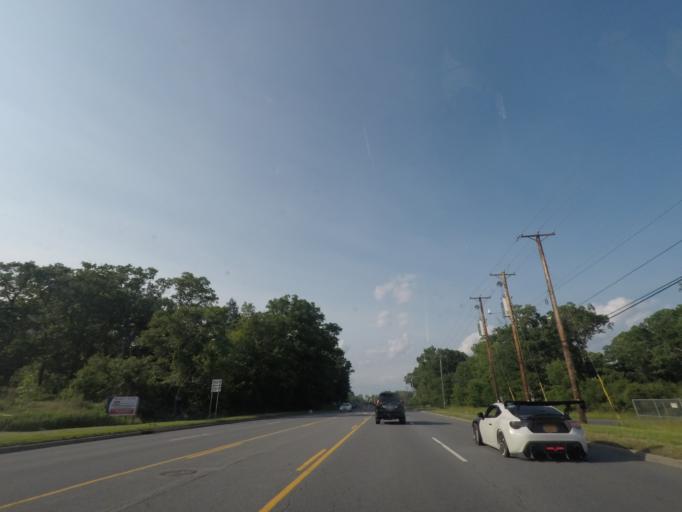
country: US
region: New York
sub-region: Orange County
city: Vails Gate
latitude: 41.4897
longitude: -74.0770
